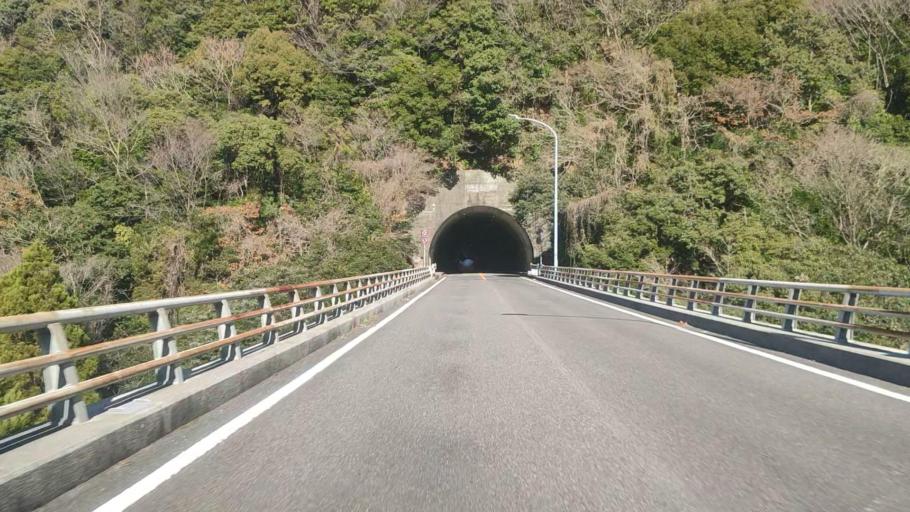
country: JP
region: Oita
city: Saiki
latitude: 32.8917
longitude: 131.9416
